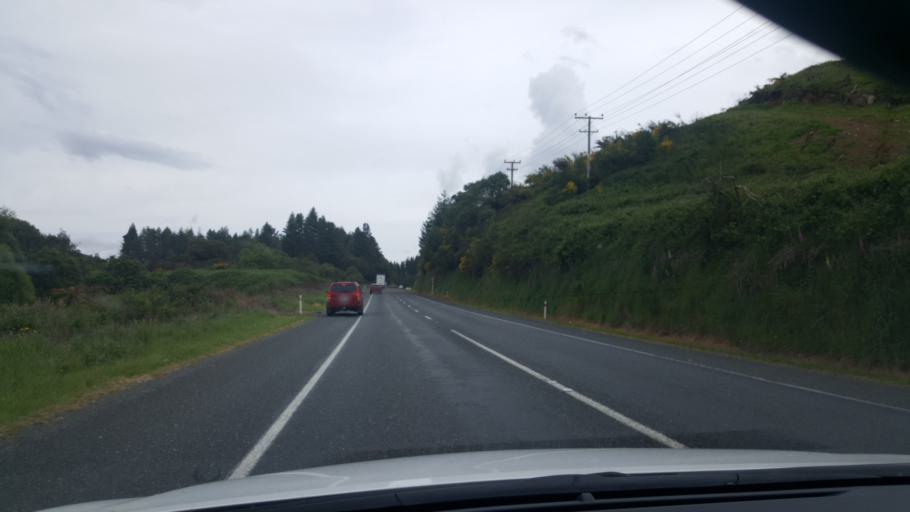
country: NZ
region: Bay of Plenty
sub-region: Rotorua District
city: Rotorua
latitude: -38.3204
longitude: 176.3734
